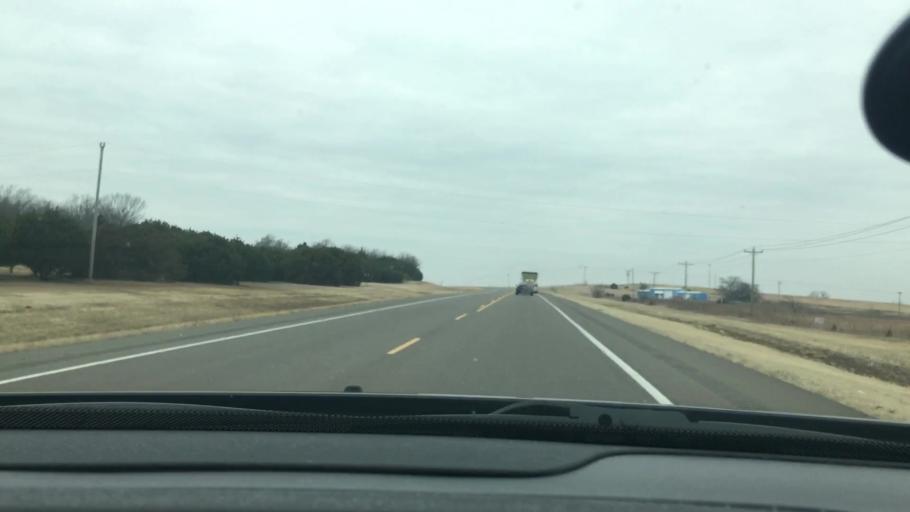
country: US
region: Oklahoma
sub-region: Murray County
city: Davis
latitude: 34.5182
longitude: -97.2083
